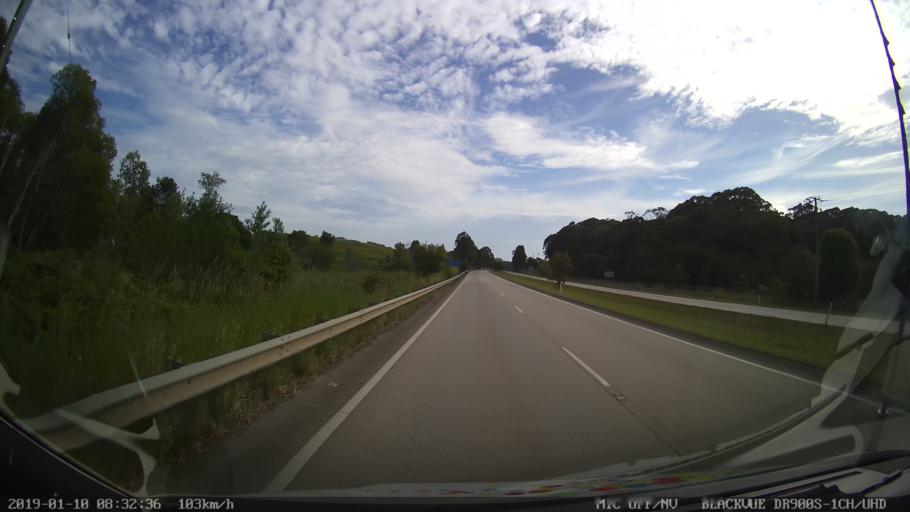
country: AU
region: New South Wales
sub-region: Coffs Harbour
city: Boambee
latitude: -30.3417
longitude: 153.0722
